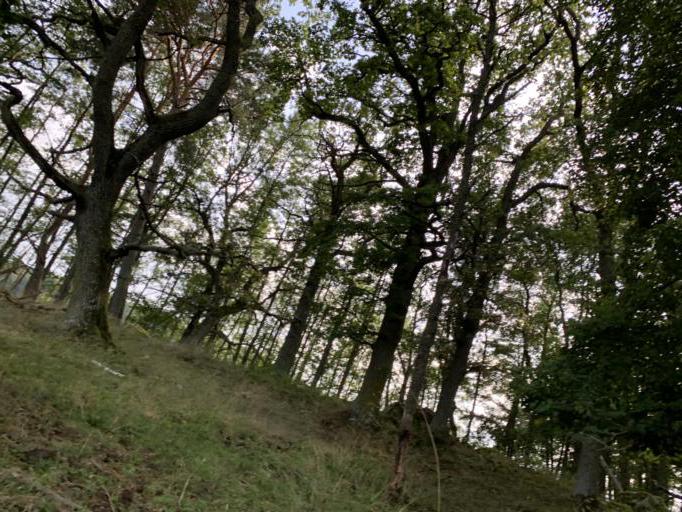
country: SE
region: Vaestmanland
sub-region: Hallstahammars Kommun
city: Kolback
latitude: 59.4683
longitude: 16.2198
